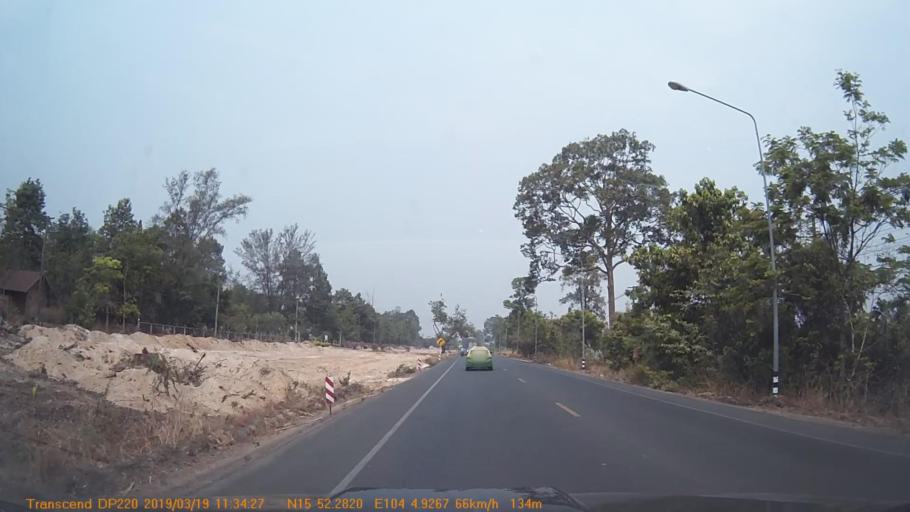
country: TH
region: Yasothon
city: Yasothon
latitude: 15.8717
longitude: 104.0819
